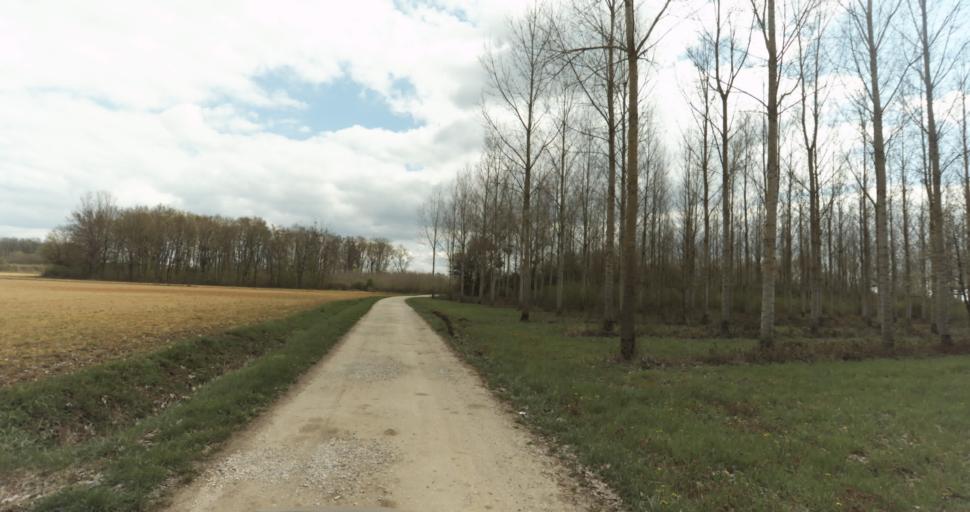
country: FR
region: Bourgogne
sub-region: Departement de la Cote-d'Or
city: Auxonne
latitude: 47.1626
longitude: 5.3975
